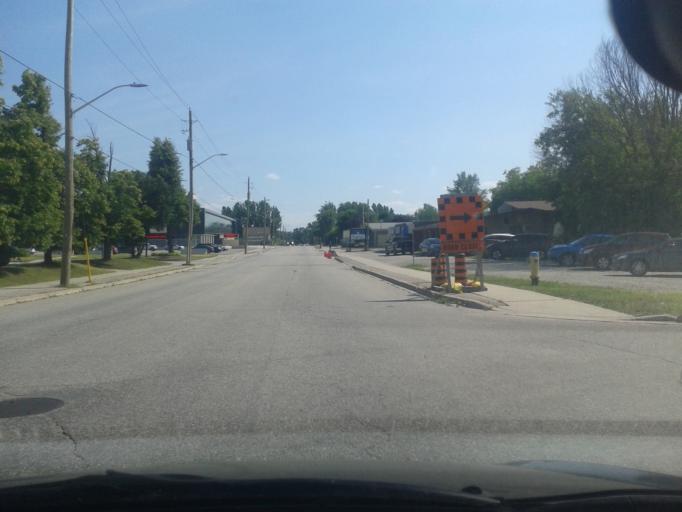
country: CA
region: Ontario
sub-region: Nipissing District
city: North Bay
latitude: 46.3163
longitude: -79.4498
